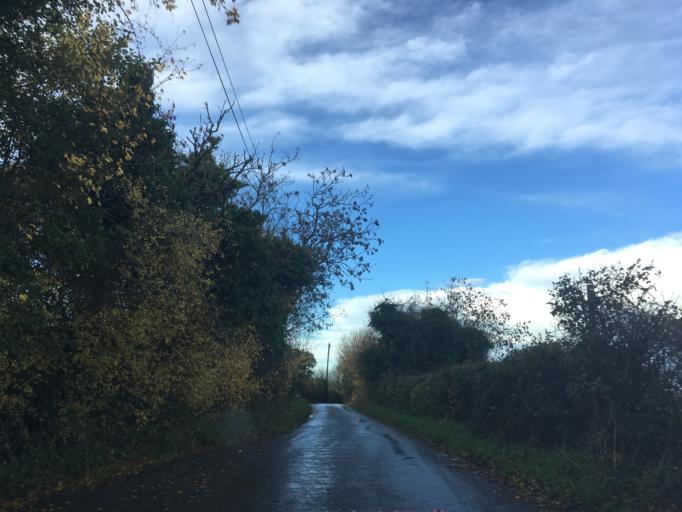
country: GB
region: England
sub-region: South Gloucestershire
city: Siston
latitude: 51.4905
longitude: -2.4526
